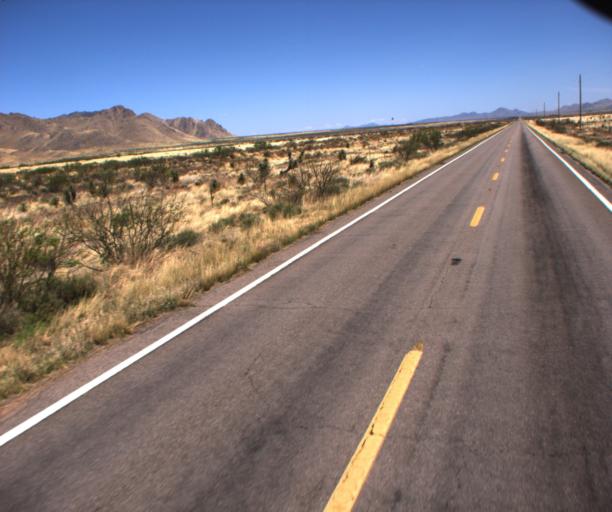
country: US
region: Arizona
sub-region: Cochise County
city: Douglas
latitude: 31.7031
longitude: -109.1241
